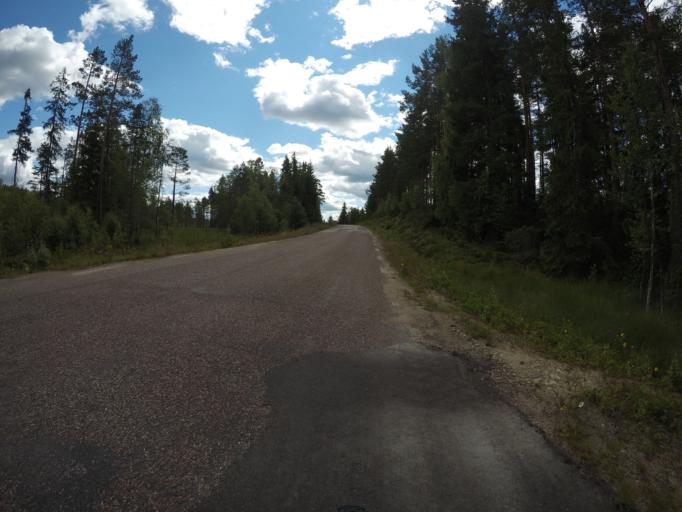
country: SE
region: OErebro
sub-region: Hallefors Kommun
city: Haellefors
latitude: 60.0640
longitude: 14.4931
